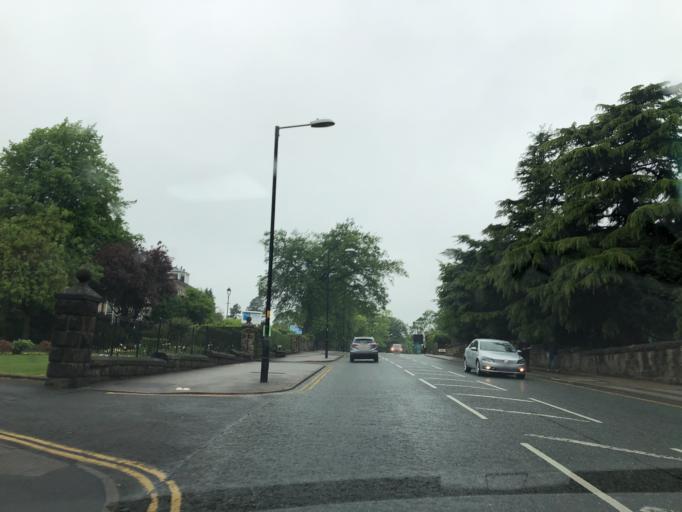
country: GB
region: England
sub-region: North Yorkshire
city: Harrogate
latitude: 53.9966
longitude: -1.5457
